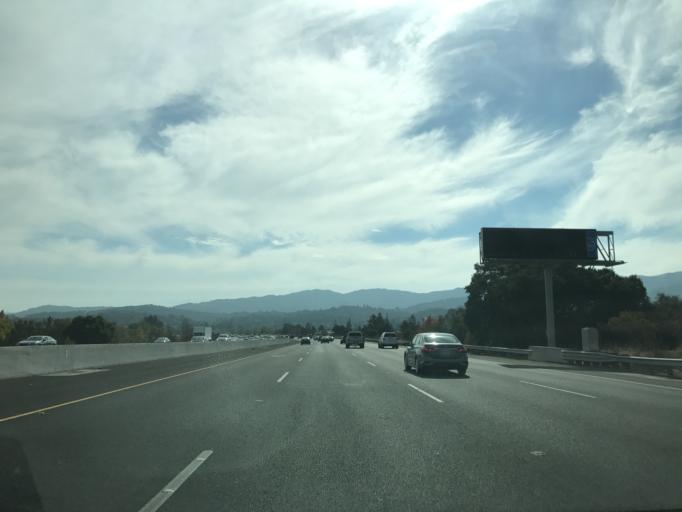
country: US
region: California
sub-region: Marin County
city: Novato
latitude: 38.1006
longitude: -122.5619
